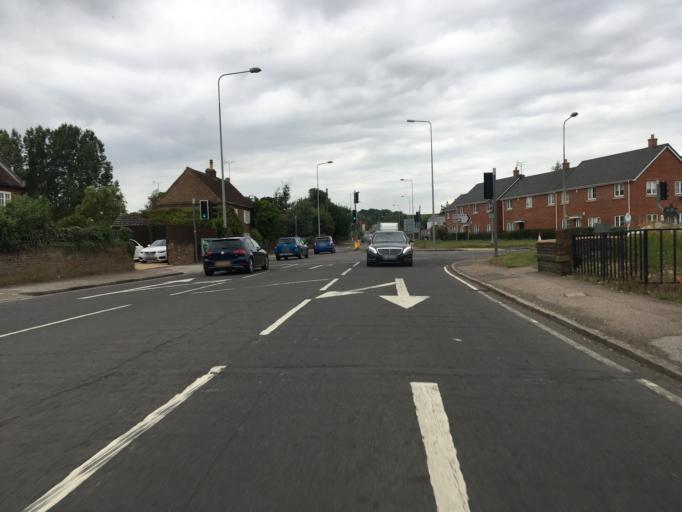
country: GB
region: England
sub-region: Central Bedfordshire
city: Hockliffe
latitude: 51.9311
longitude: -0.5863
